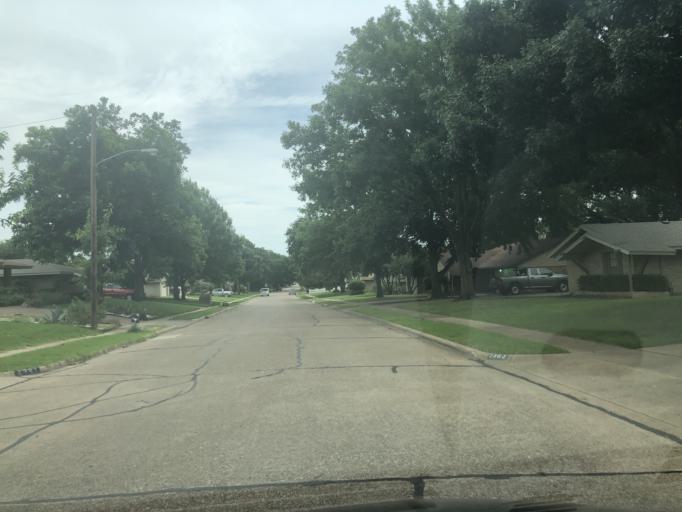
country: US
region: Texas
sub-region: Dallas County
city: Irving
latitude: 32.7966
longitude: -96.9758
